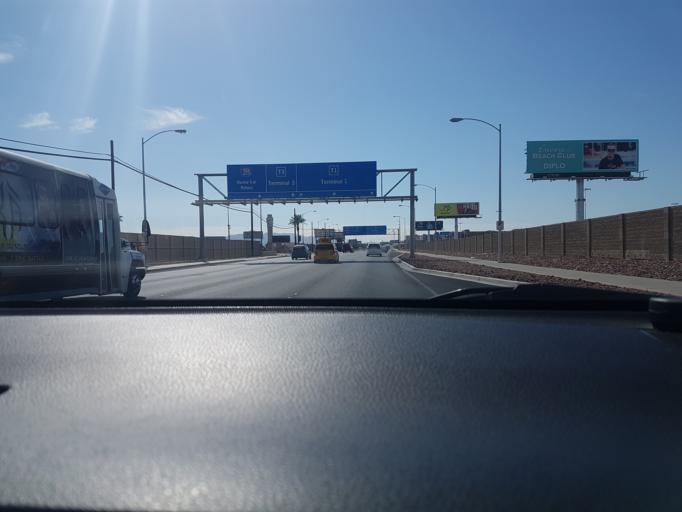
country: US
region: Nevada
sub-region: Clark County
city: Paradise
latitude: 36.0973
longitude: -115.1488
